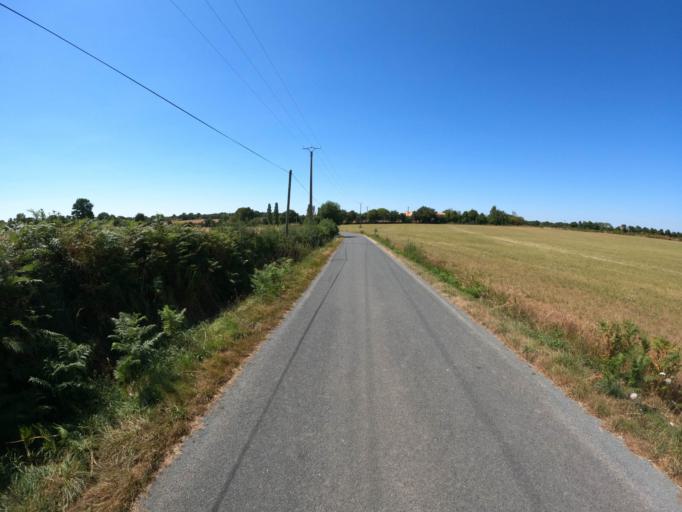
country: FR
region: Pays de la Loire
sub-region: Departement de Maine-et-Loire
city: Saint-Christophe-du-Bois
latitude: 47.0475
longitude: -0.9599
